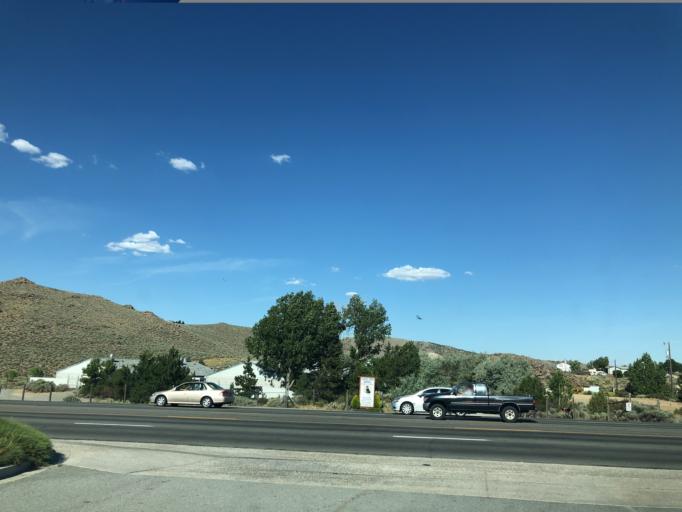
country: US
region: Nevada
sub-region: Washoe County
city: Lemmon Valley
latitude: 39.6163
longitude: -119.8485
